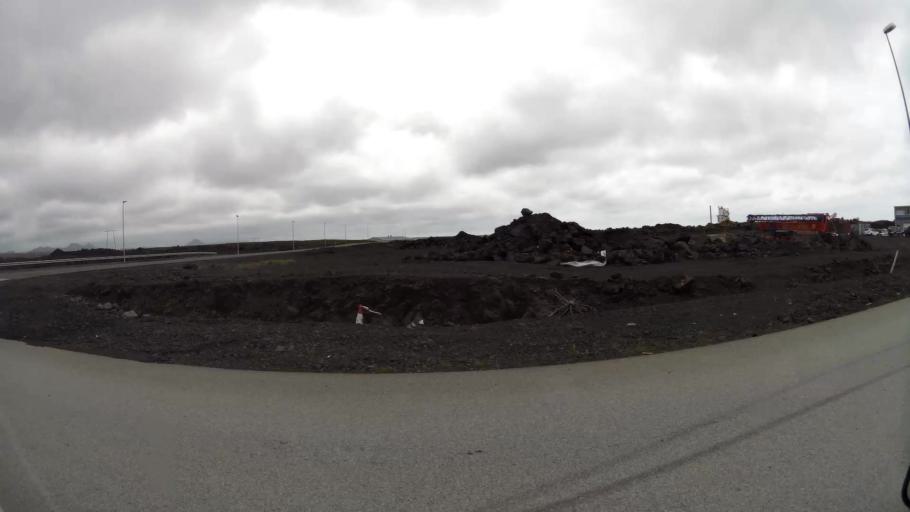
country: IS
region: Capital Region
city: Alftanes
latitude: 64.0381
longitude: -21.9998
